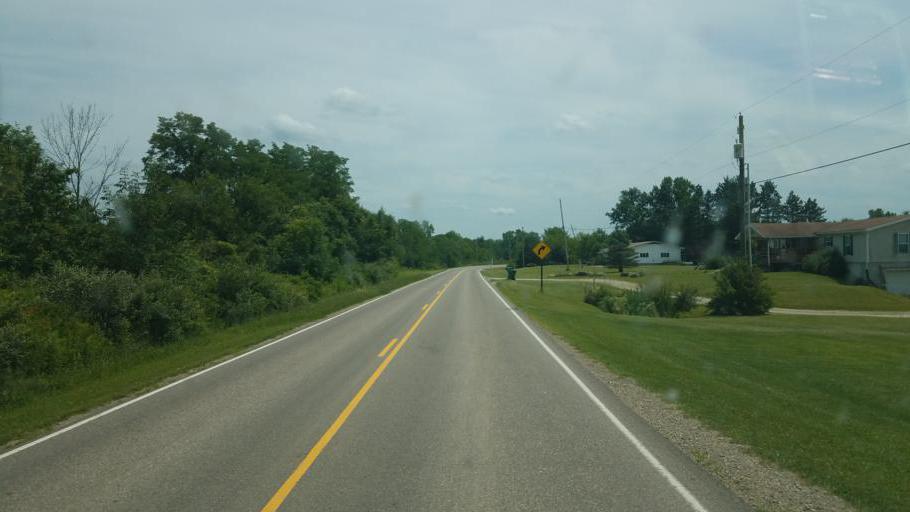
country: US
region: Ohio
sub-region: Knox County
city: Fredericktown
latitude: 40.5212
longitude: -82.5924
